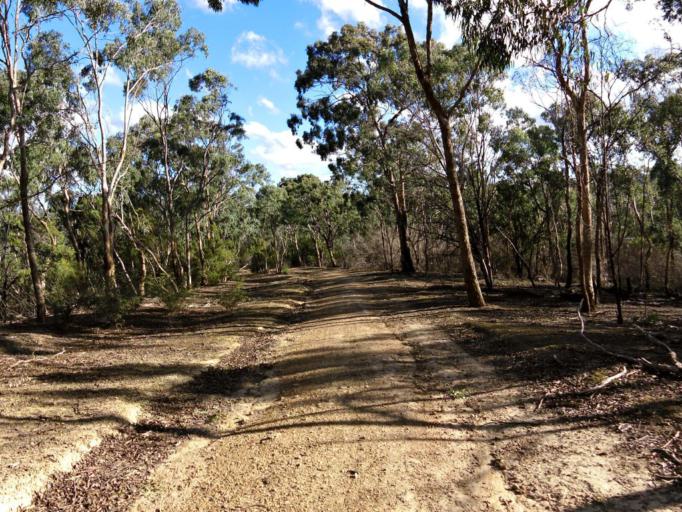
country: AU
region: Victoria
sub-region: Nillumbik
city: North Warrandyte
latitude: -37.7366
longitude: 145.2022
